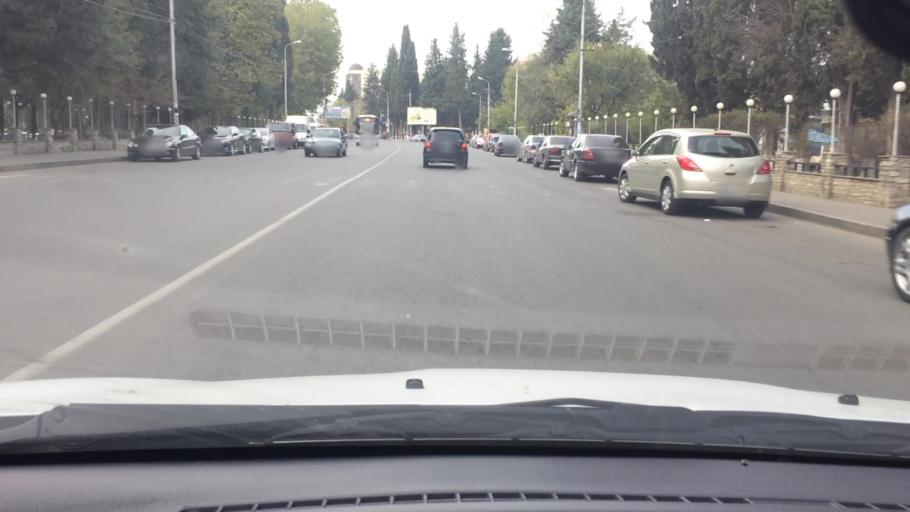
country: GE
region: Kvemo Kartli
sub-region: Marneuli
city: Marneuli
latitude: 41.4724
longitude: 44.8150
